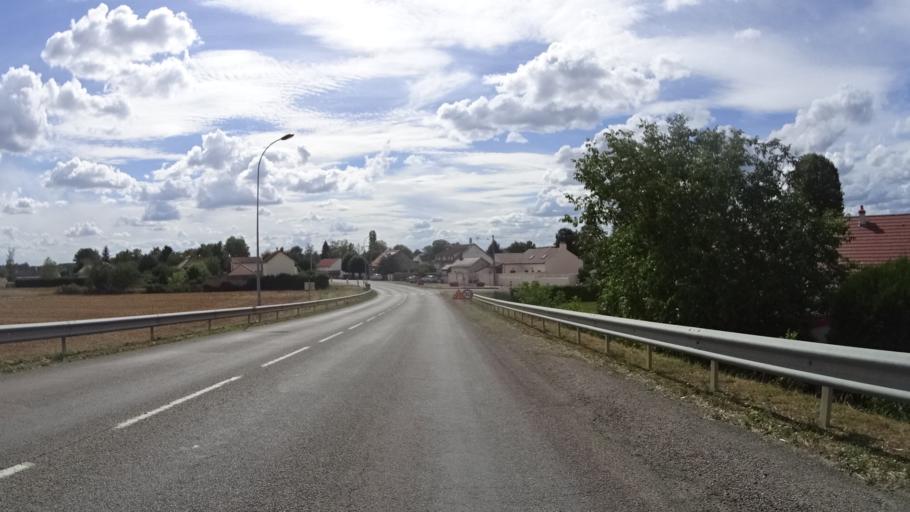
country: FR
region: Bourgogne
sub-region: Departement de la Cote-d'Or
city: Losne
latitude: 47.0864
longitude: 5.2544
